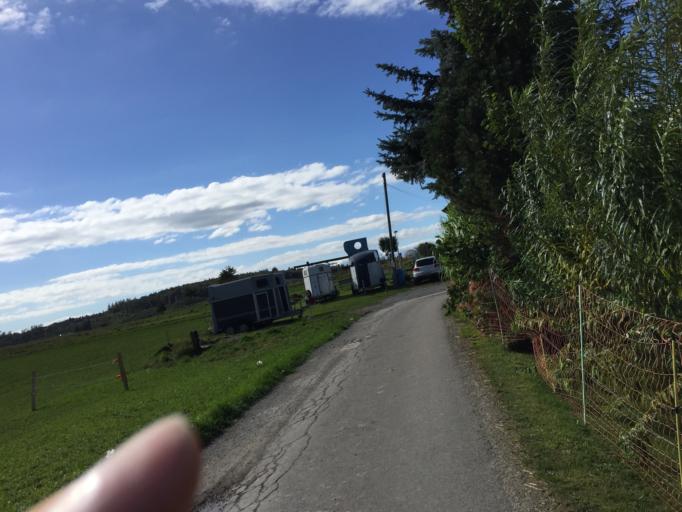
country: CH
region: Bern
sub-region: Bern-Mittelland District
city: Koniz
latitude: 46.9228
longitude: 7.4228
